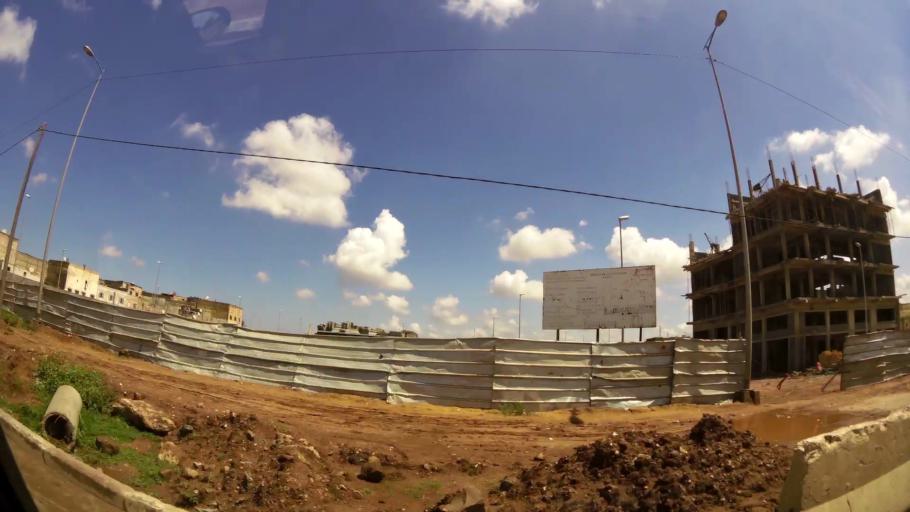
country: MA
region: Grand Casablanca
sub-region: Mediouna
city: Tit Mellil
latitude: 33.5416
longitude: -7.5417
